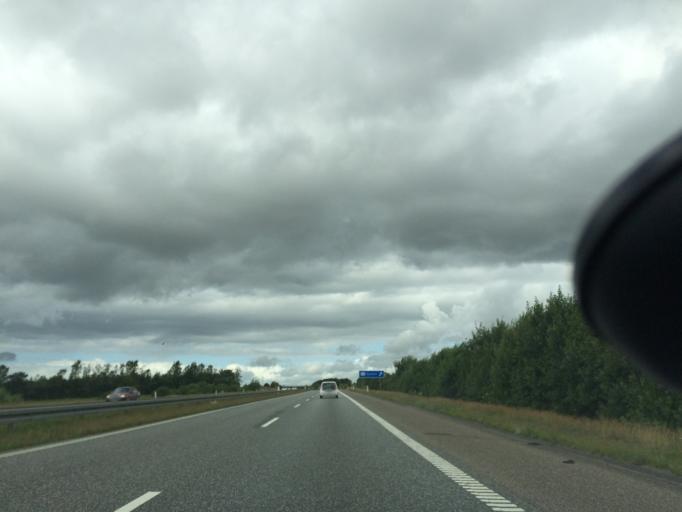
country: DK
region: Central Jutland
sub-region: Skanderborg Kommune
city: Galten
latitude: 56.1432
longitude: 9.9282
